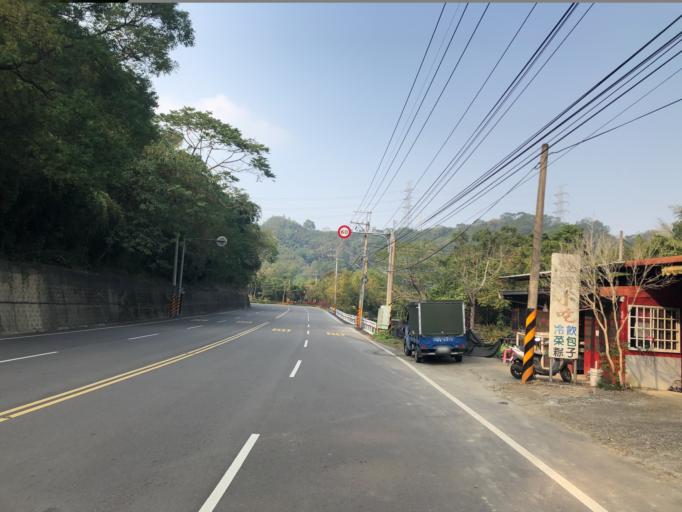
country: TW
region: Taiwan
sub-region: Miaoli
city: Miaoli
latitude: 24.6125
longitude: 120.9582
